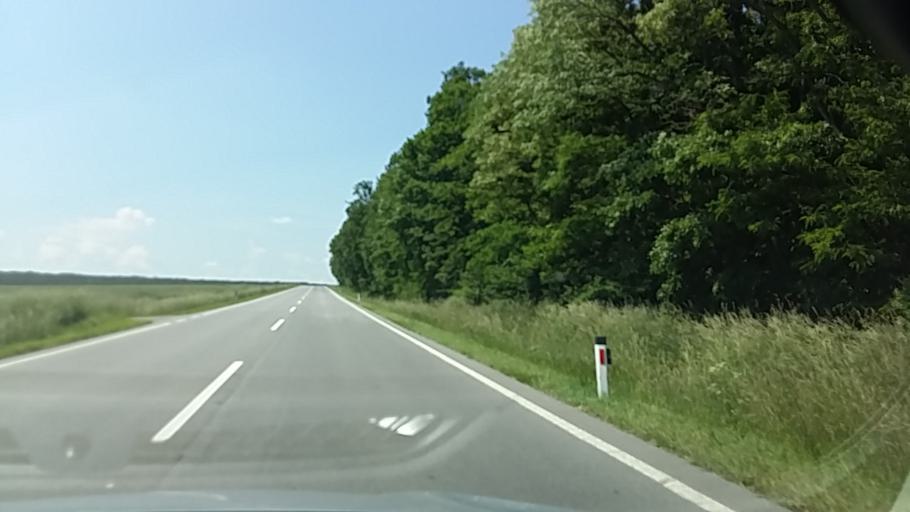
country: AT
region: Burgenland
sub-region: Politischer Bezirk Oberpullendorf
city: Raiding
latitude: 47.5311
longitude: 16.5299
